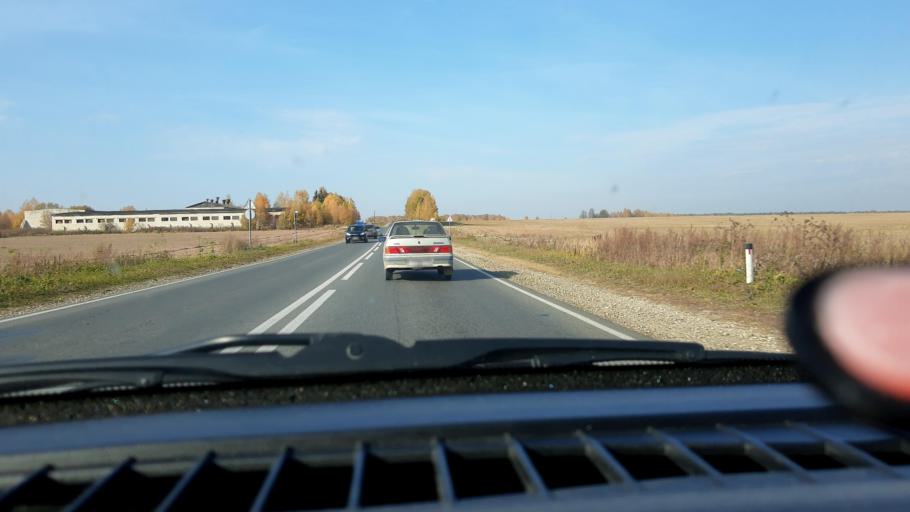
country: RU
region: Nizjnij Novgorod
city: Gorodets
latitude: 56.6227
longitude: 43.5513
